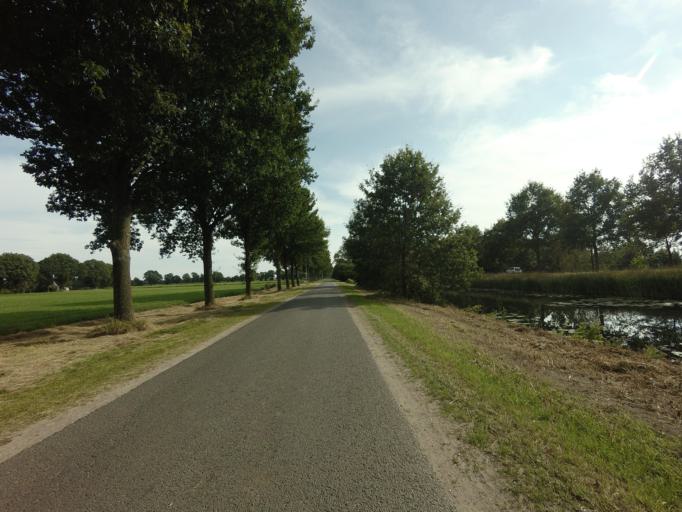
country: NL
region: Drenthe
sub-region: Gemeente Coevorden
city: Coevorden
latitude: 52.6871
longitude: 6.7114
